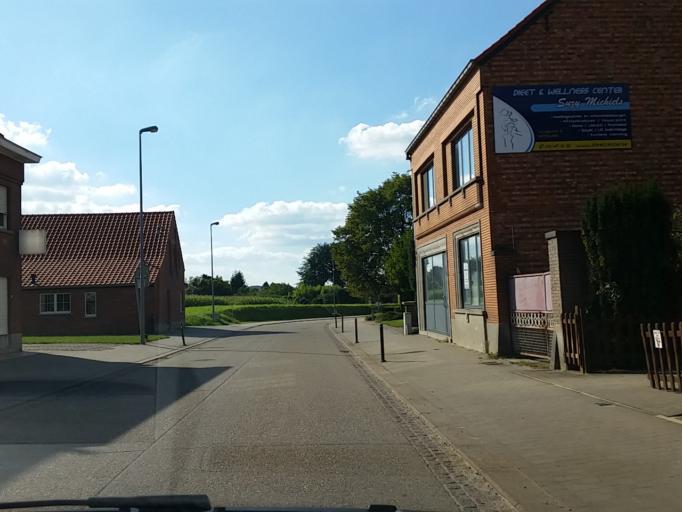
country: BE
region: Flanders
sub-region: Provincie Vlaams-Brabant
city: Holsbeek
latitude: 50.9258
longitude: 4.8035
